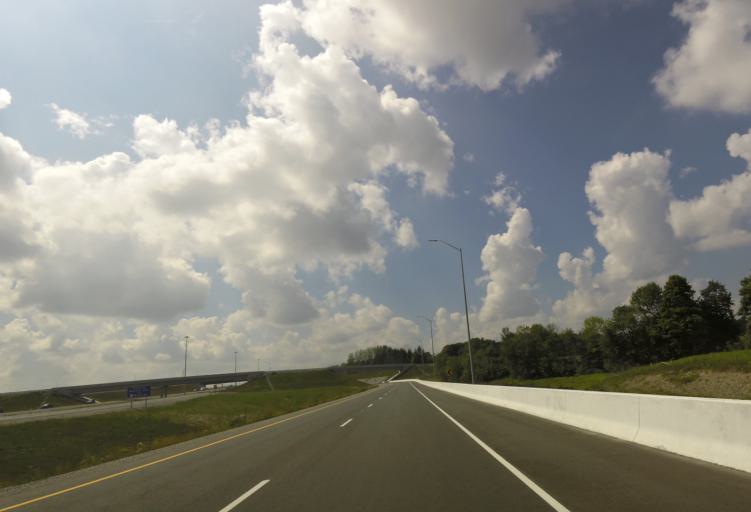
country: CA
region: Ontario
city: Ajax
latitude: 43.9518
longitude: -79.0022
